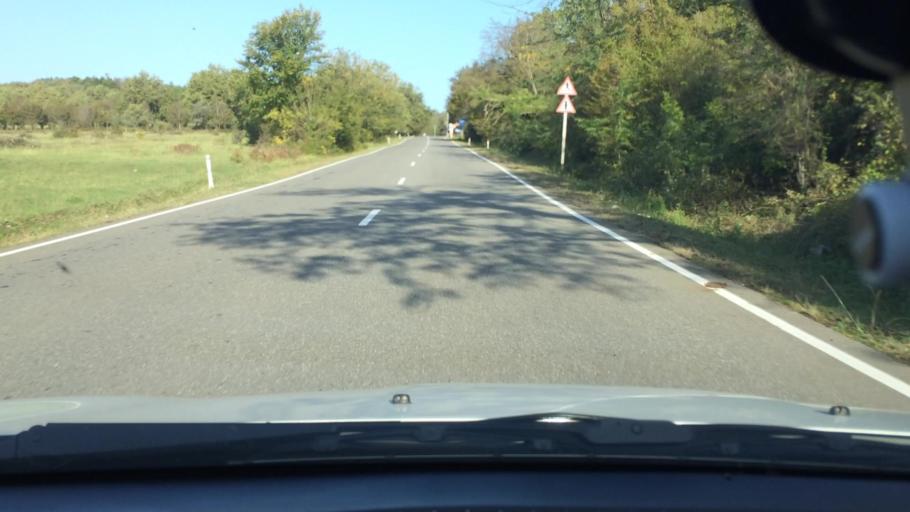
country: GE
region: Imereti
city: Kutaisi
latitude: 42.2442
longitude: 42.7606
